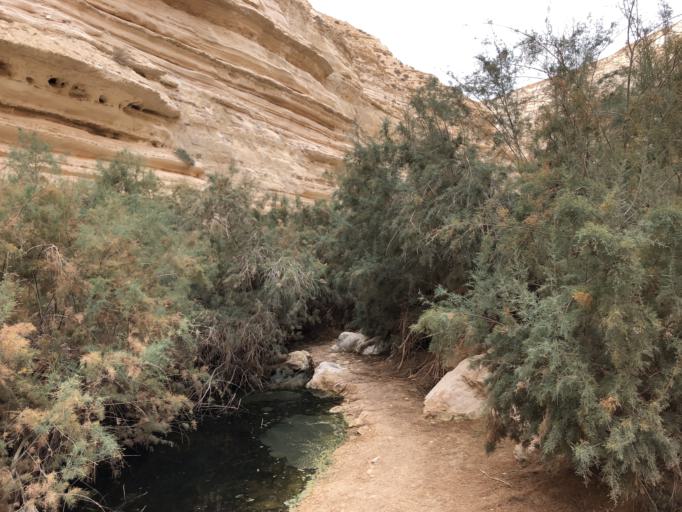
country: IL
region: Southern District
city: Midreshet Ben-Gurion
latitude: 30.8271
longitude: 34.7656
